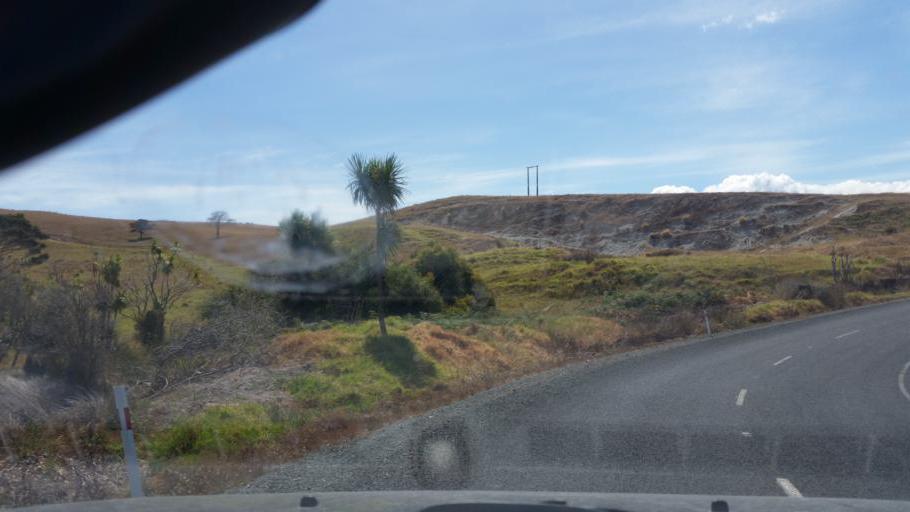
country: NZ
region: Northland
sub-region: Kaipara District
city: Dargaville
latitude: -36.1700
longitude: 174.1649
